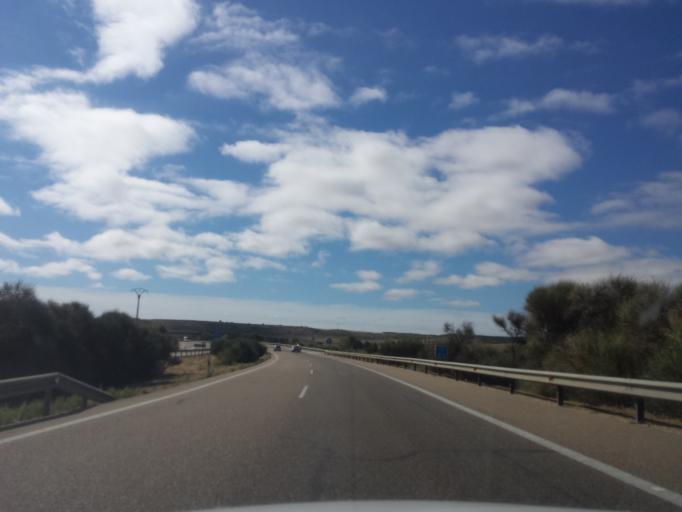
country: ES
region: Castille and Leon
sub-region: Provincia de Valladolid
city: Villardefrades
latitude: 41.7200
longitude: -5.2478
